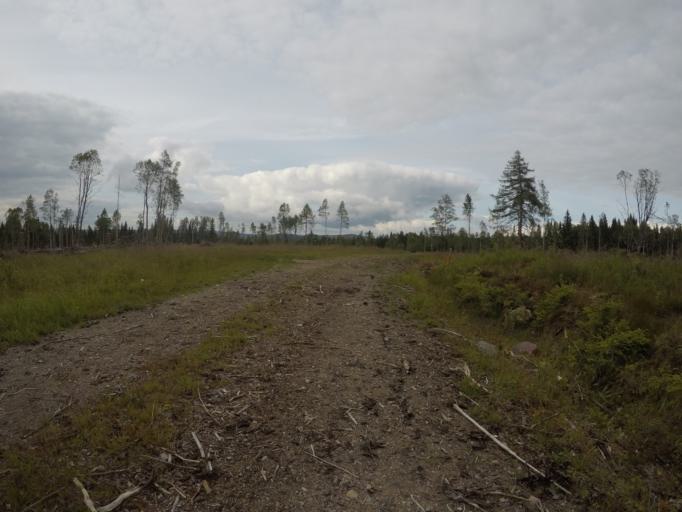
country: SE
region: Vaermland
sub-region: Filipstads Kommun
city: Lesjofors
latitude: 60.2027
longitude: 14.2613
